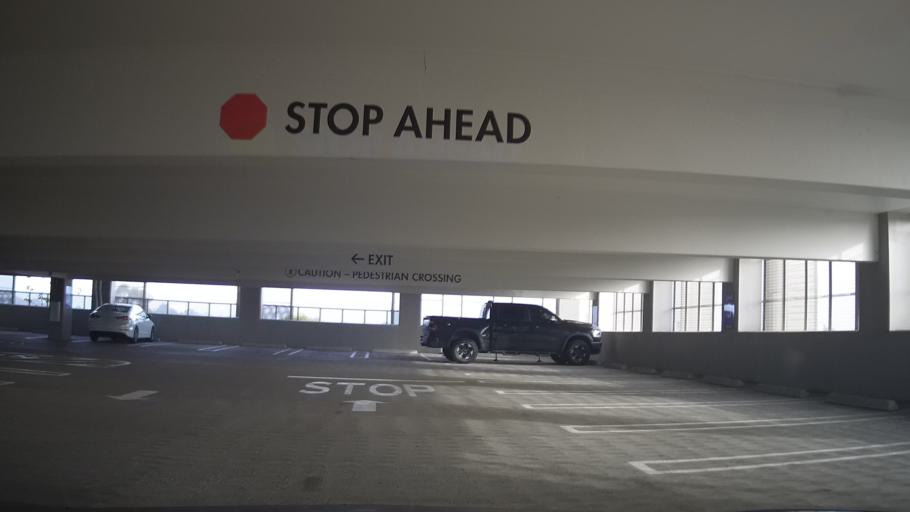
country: US
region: California
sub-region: San Diego County
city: La Mesa
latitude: 32.8304
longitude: -117.1237
